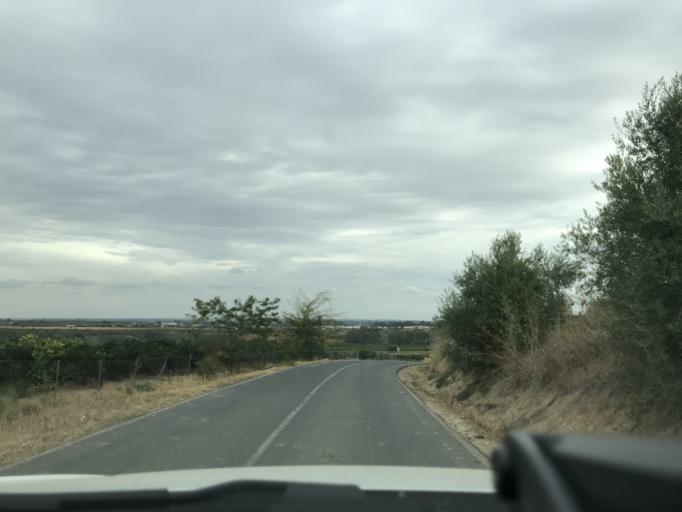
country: ES
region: Andalusia
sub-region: Provincia de Sevilla
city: Villanueva del Rio y Minas
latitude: 37.6386
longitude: -5.7022
